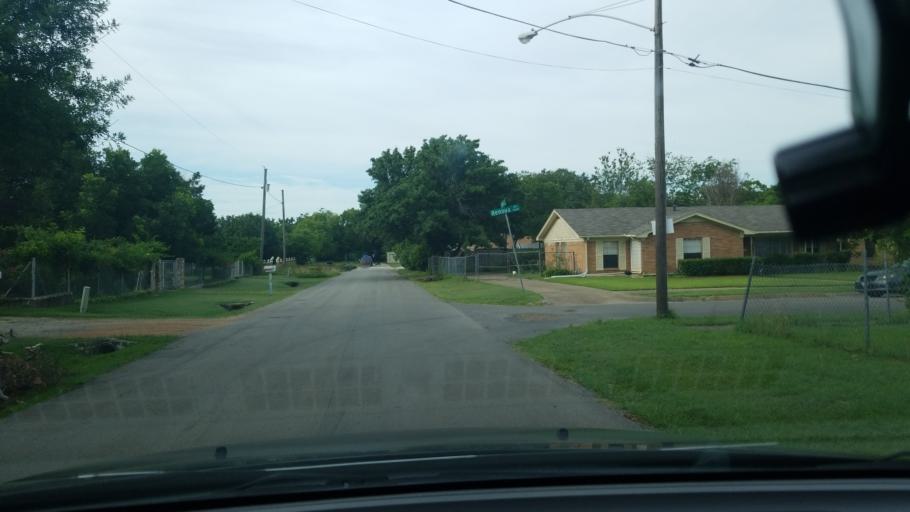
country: US
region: Texas
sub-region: Dallas County
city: Balch Springs
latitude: 32.7574
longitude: -96.6619
